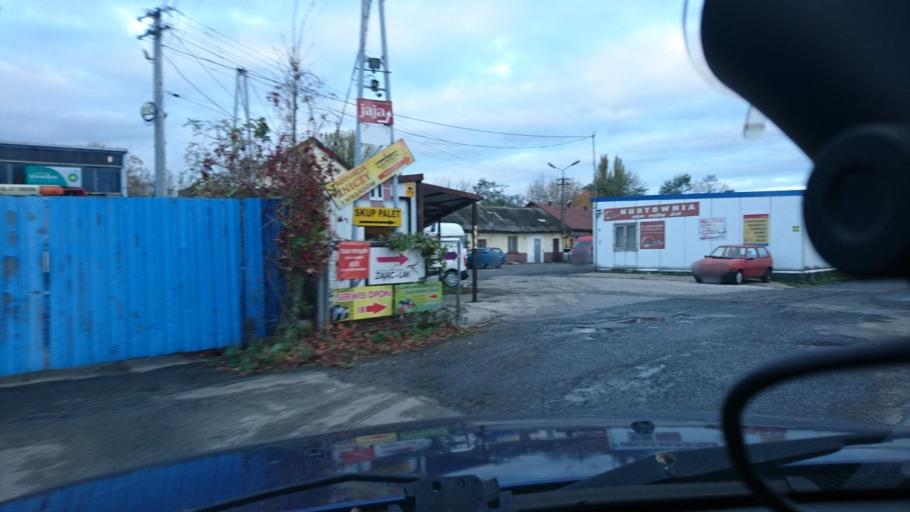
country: PL
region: Silesian Voivodeship
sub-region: Bielsko-Biala
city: Bielsko-Biala
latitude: 49.8340
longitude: 19.0522
